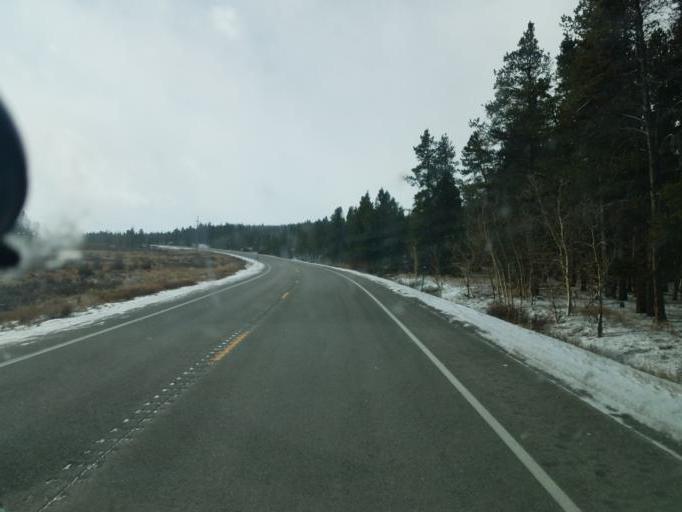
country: US
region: Colorado
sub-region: Summit County
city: Breckenridge
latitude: 39.4224
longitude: -105.7652
